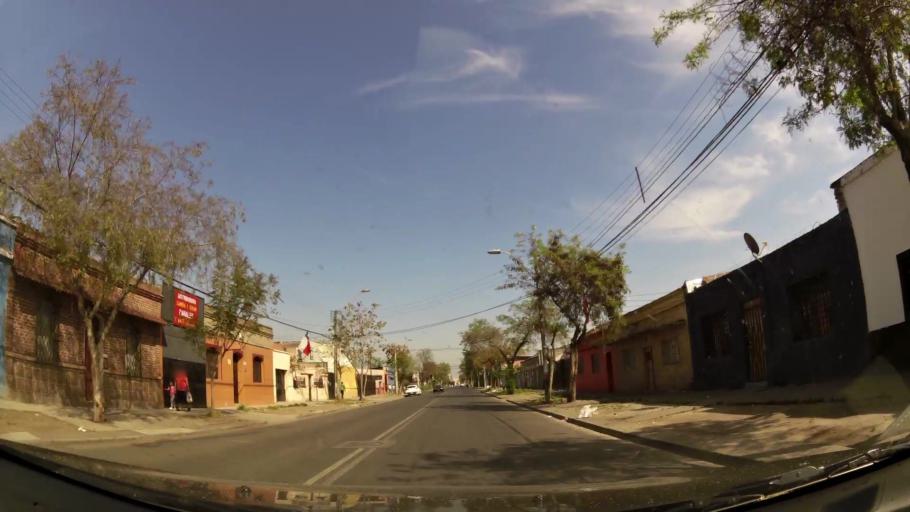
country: CL
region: Santiago Metropolitan
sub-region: Provincia de Santiago
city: Santiago
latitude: -33.4064
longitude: -70.6381
